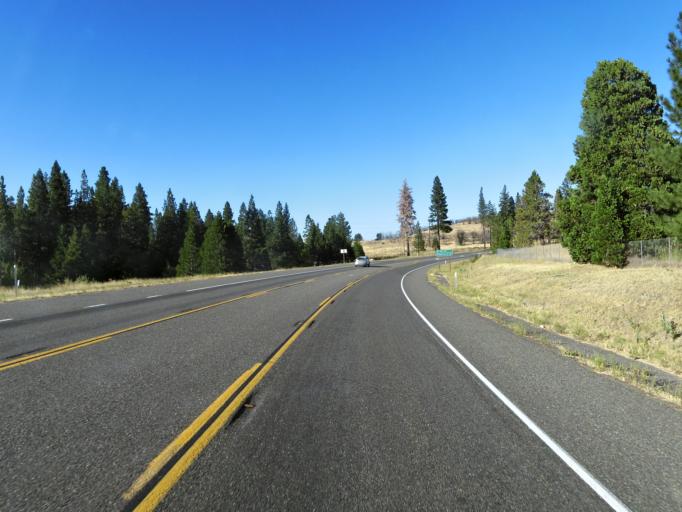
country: US
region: California
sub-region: Siskiyou County
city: Weed
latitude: 41.4389
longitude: -122.3872
